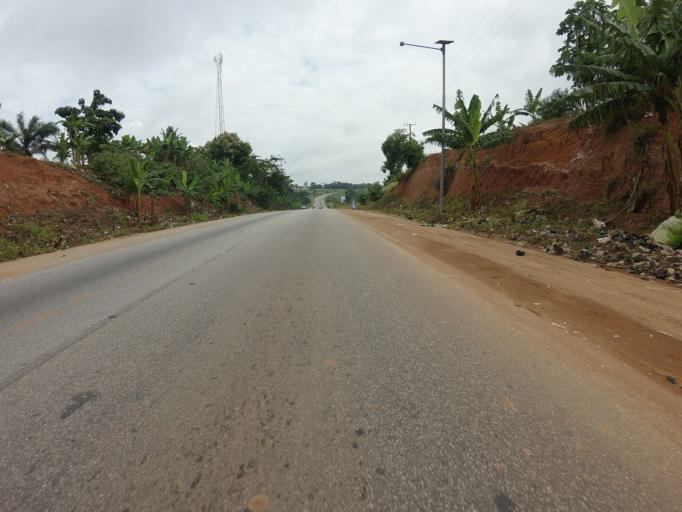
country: GH
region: Ashanti
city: Tafo
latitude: 6.9693
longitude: -1.6826
